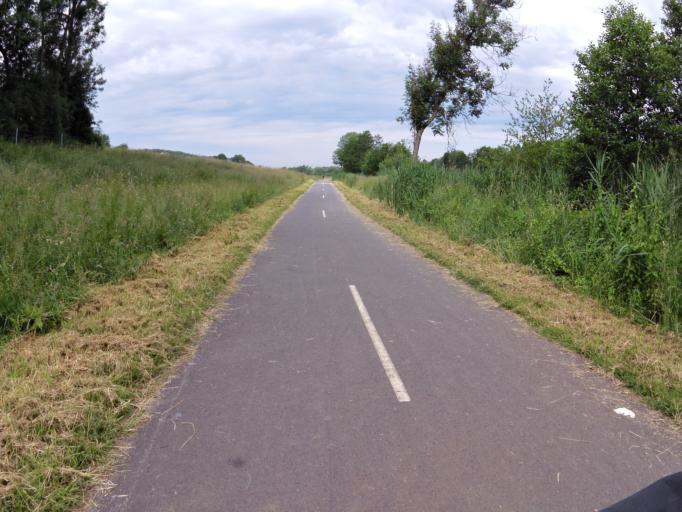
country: FR
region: Champagne-Ardenne
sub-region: Departement des Ardennes
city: Donchery
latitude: 49.6924
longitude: 4.8882
